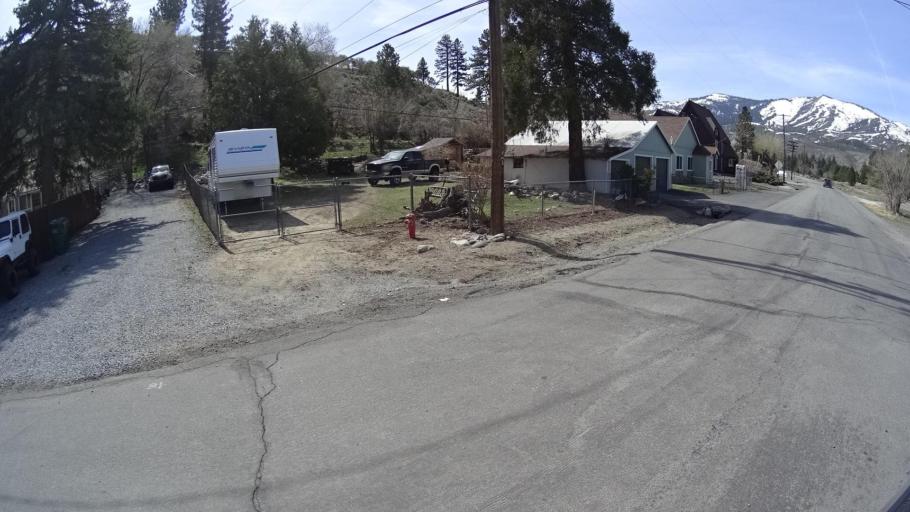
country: US
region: Nevada
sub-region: Washoe County
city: Verdi
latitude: 39.5170
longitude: -119.9885
